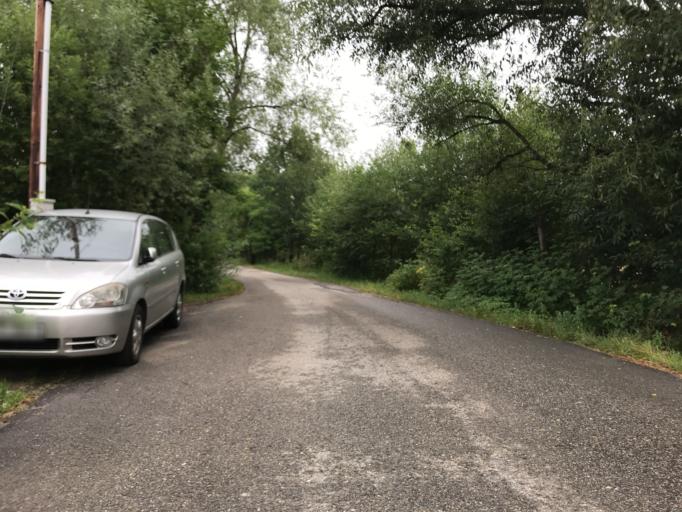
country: CZ
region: Jihocesky
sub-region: Okres Jindrichuv Hradec
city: Trebon
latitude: 49.0078
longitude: 14.7658
